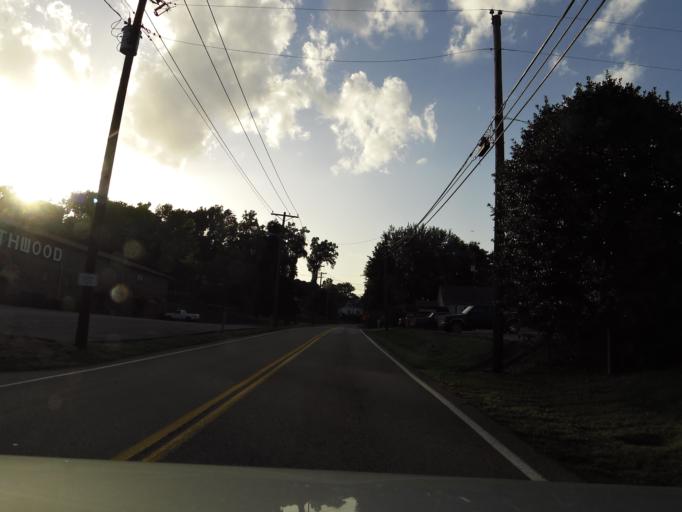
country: US
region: Tennessee
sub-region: Knox County
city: Knoxville
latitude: 35.9540
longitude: -83.8958
